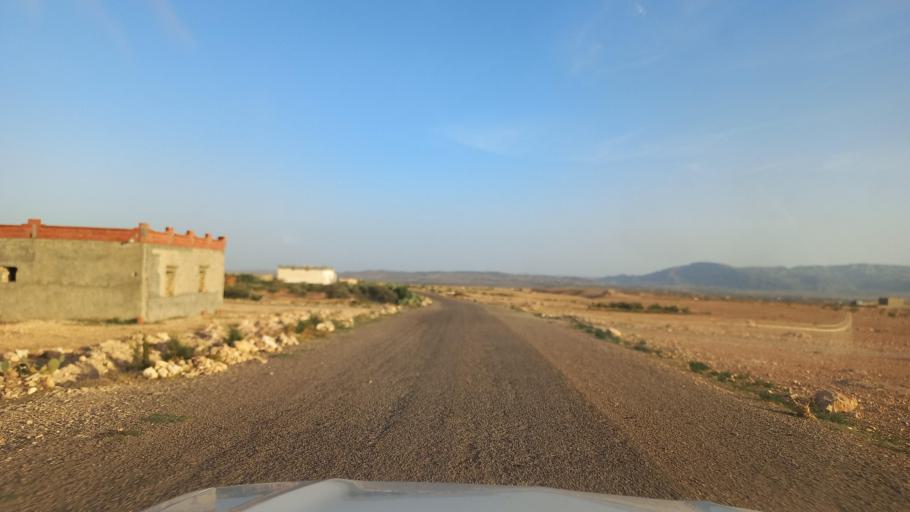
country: TN
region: Al Qasrayn
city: Kasserine
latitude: 35.2769
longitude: 8.9109
